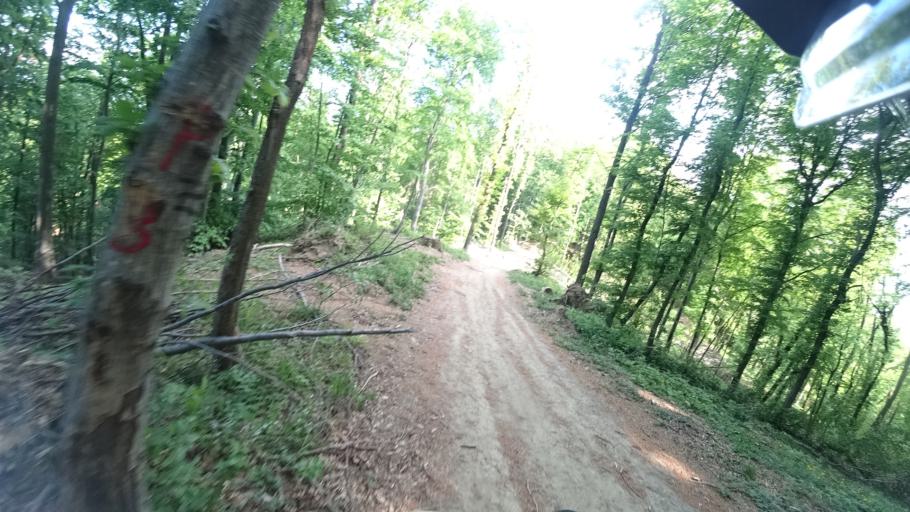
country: HR
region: Zagrebacka
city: Jablanovec
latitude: 45.8591
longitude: 15.8855
